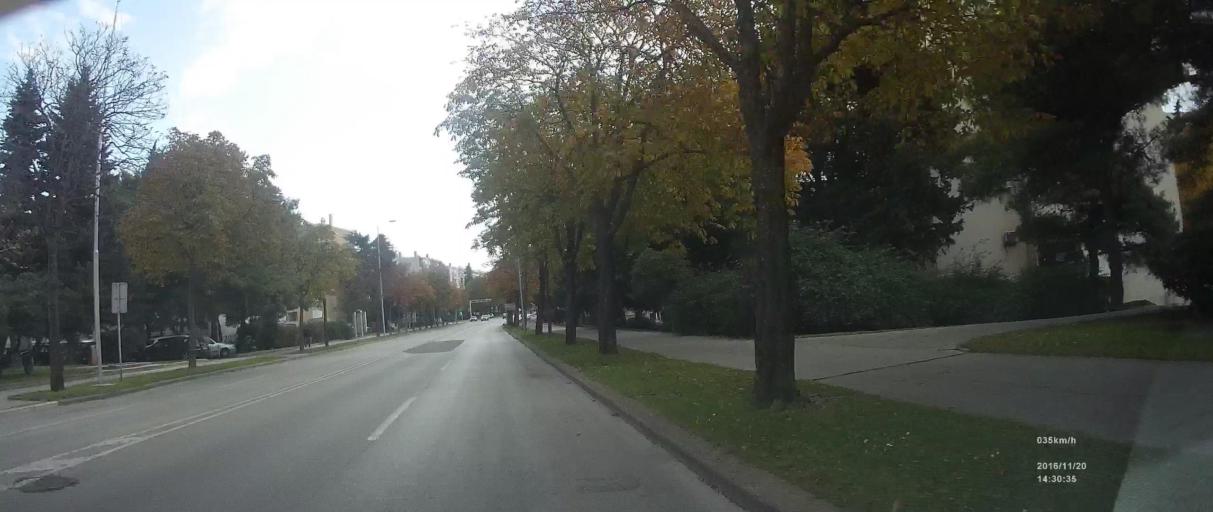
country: HR
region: Splitsko-Dalmatinska
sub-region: Grad Split
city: Split
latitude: 43.5151
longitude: 16.4524
